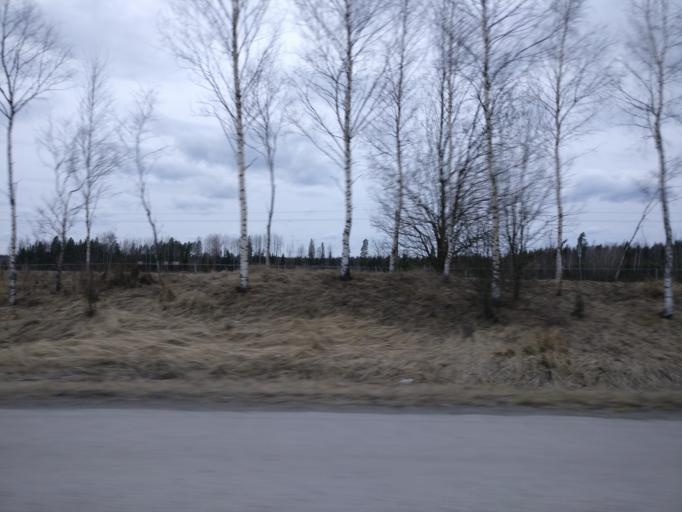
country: FI
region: Uusimaa
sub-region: Helsinki
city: Nurmijaervi
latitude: 60.4241
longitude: 24.8254
